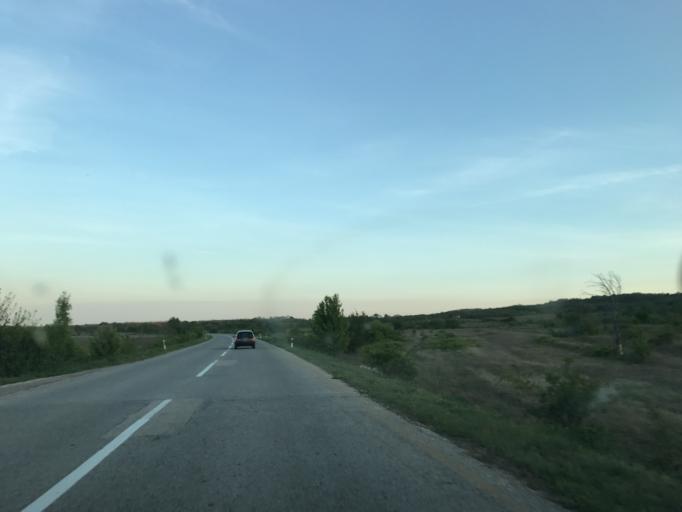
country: RO
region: Mehedinti
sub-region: Comuna Gogosu
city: Ostrovu Mare
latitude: 44.3340
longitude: 22.4747
